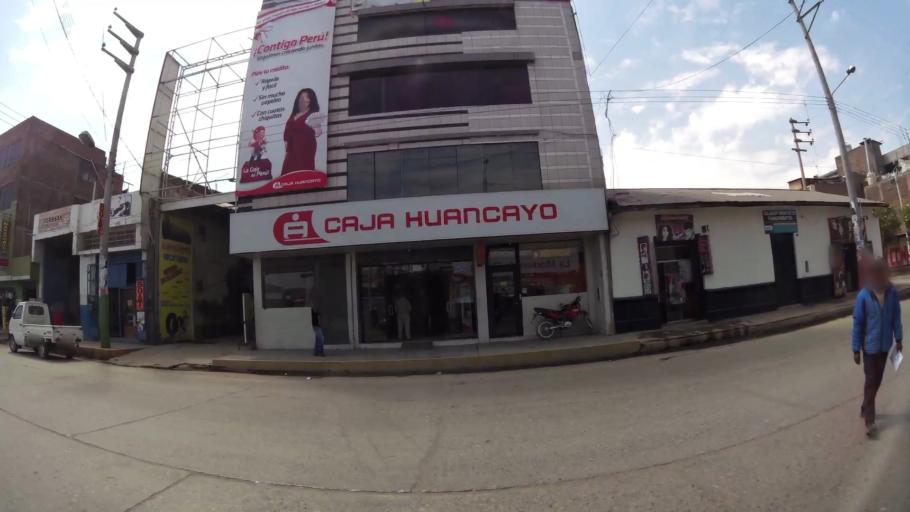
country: PE
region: Junin
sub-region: Provincia de Huancayo
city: Huancayo
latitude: -12.0806
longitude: -75.2028
